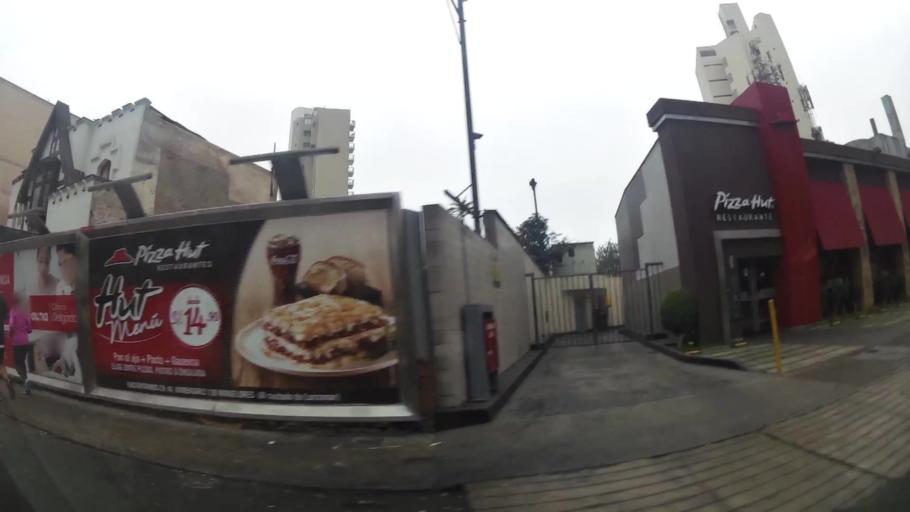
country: PE
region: Lima
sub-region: Lima
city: Surco
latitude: -12.1325
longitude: -77.0288
